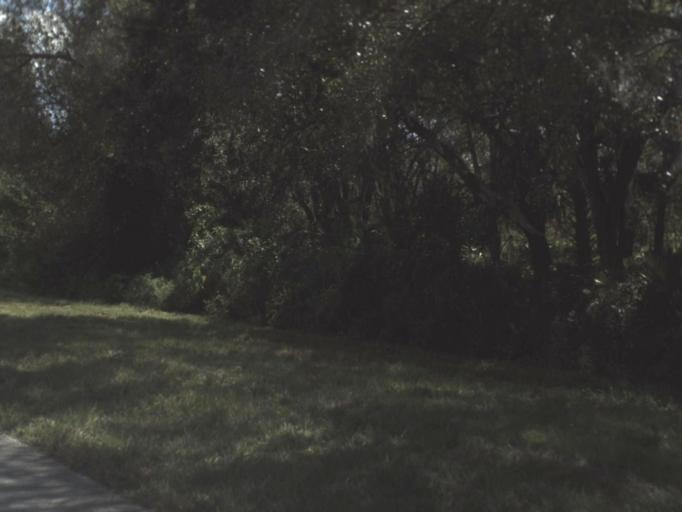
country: US
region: Florida
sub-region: Okeechobee County
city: Okeechobee
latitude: 27.3767
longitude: -80.9849
